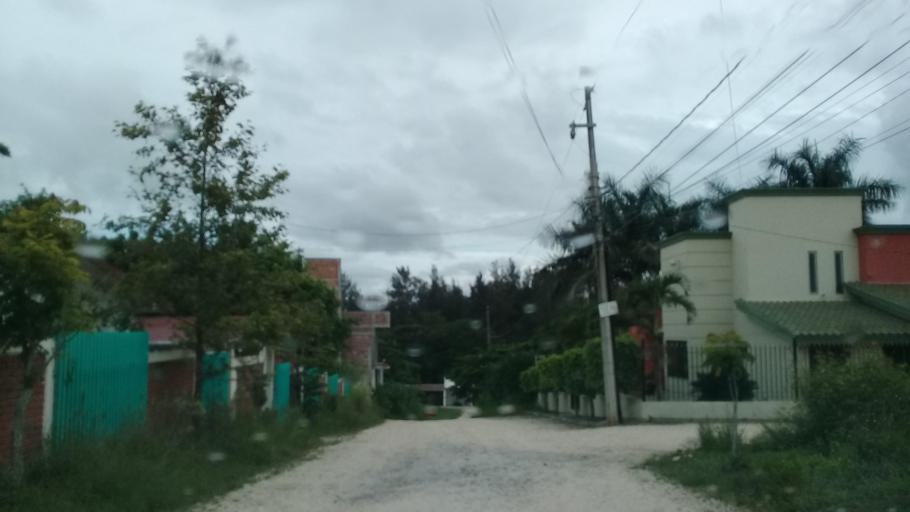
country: MX
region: Veracruz
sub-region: Emiliano Zapata
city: Jacarandas
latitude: 19.5043
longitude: -96.8406
